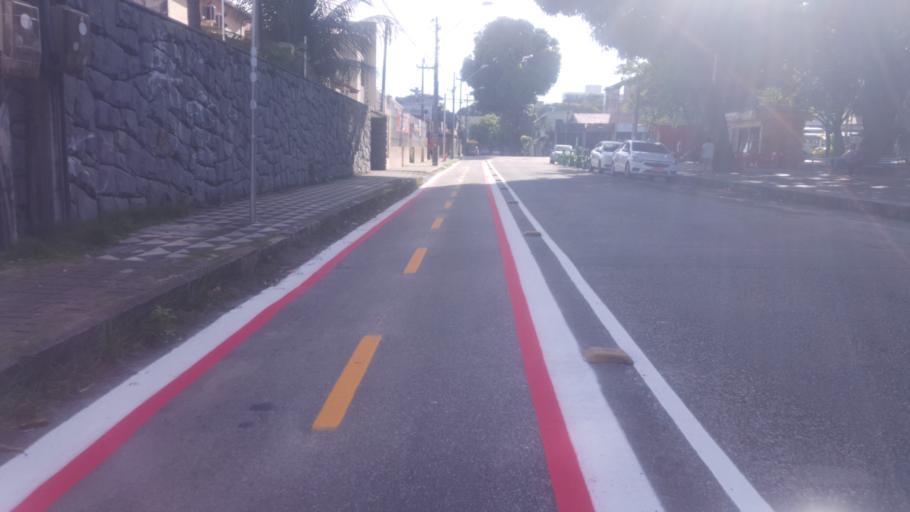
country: BR
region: Ceara
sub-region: Fortaleza
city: Fortaleza
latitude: -3.7428
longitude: -38.5378
